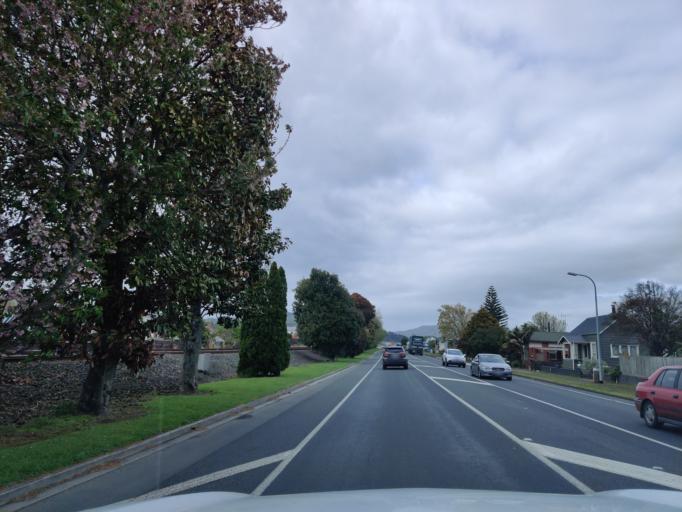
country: NZ
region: Waikato
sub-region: Waikato District
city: Ngaruawahia
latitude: -37.5498
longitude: 175.1586
